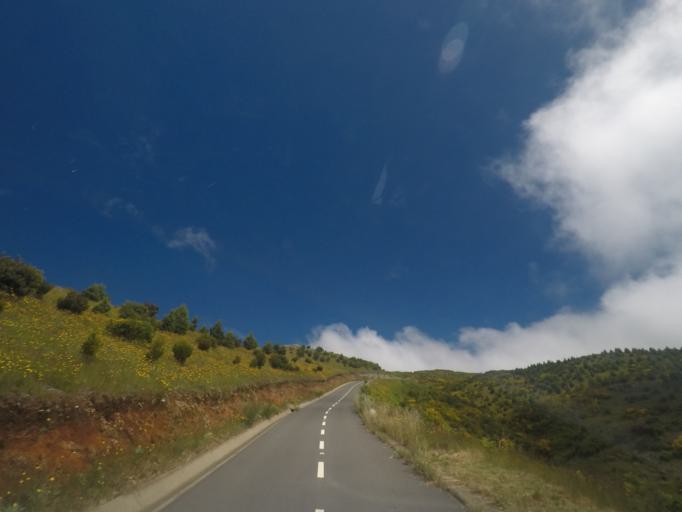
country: PT
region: Madeira
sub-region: Camara de Lobos
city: Curral das Freiras
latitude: 32.7079
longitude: -16.9393
